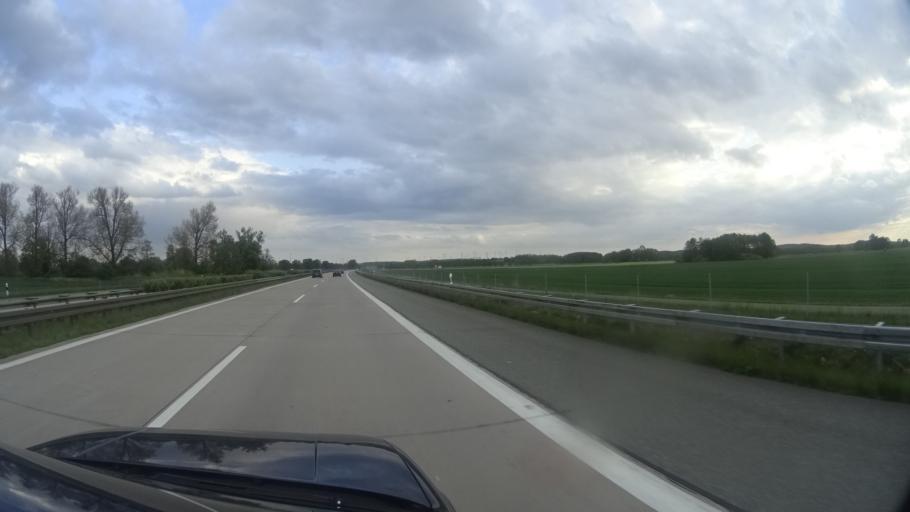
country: DE
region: Brandenburg
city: Wittstock
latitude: 53.1840
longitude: 12.4563
